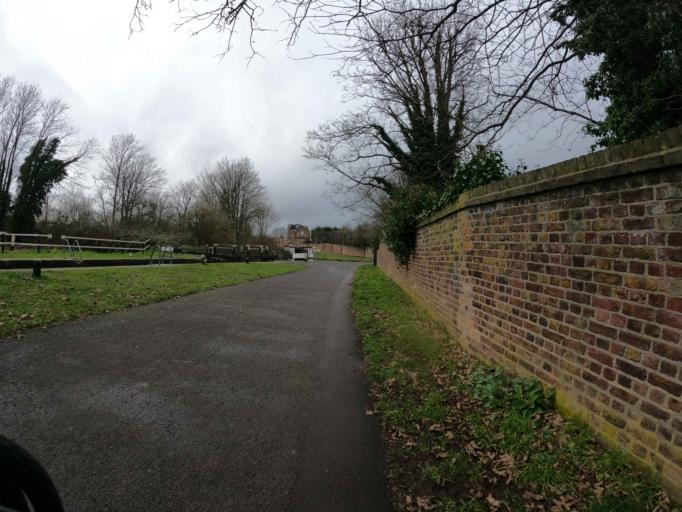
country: GB
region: England
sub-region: Greater London
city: Greenford
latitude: 51.5052
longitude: -0.3465
